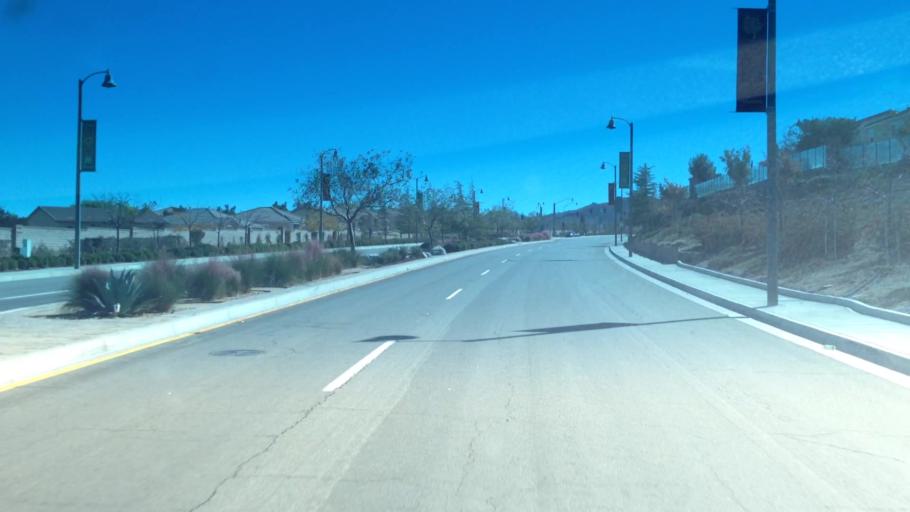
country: US
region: California
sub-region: Los Angeles County
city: Desert View Highlands
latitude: 34.5636
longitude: -118.1713
